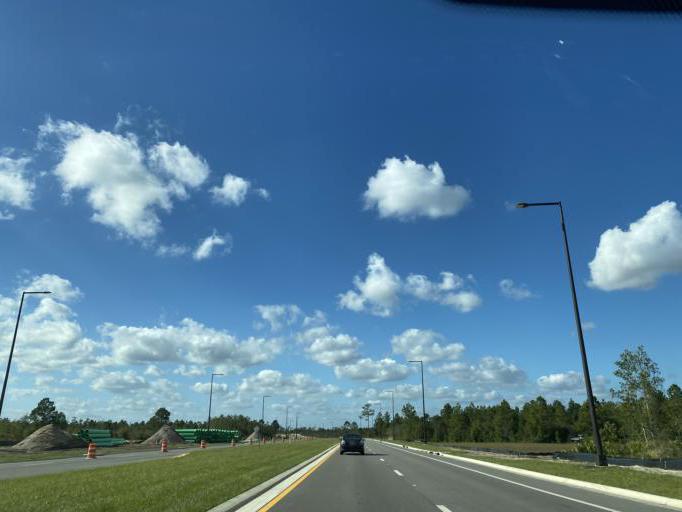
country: US
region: Florida
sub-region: Polk County
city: Citrus Ridge
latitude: 28.3794
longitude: -81.6238
